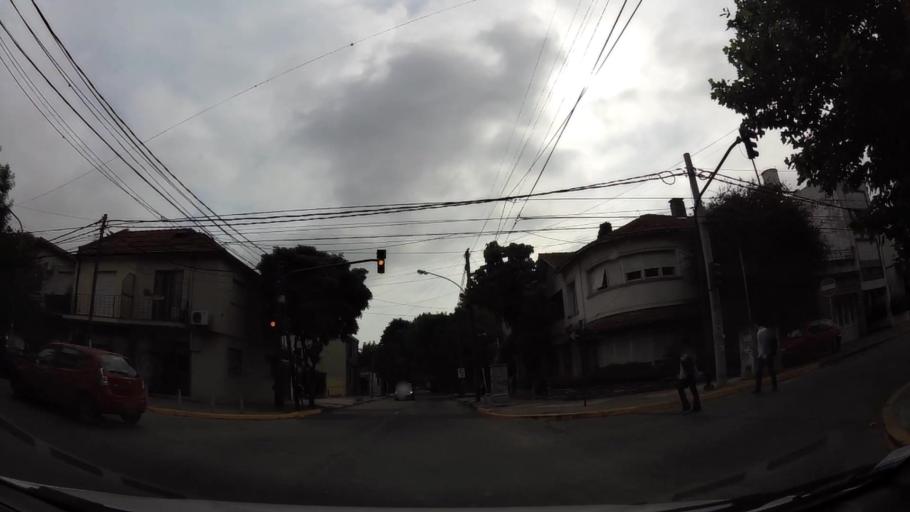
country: AR
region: Buenos Aires
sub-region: Partido de Vicente Lopez
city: Olivos
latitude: -34.5347
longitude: -58.4760
